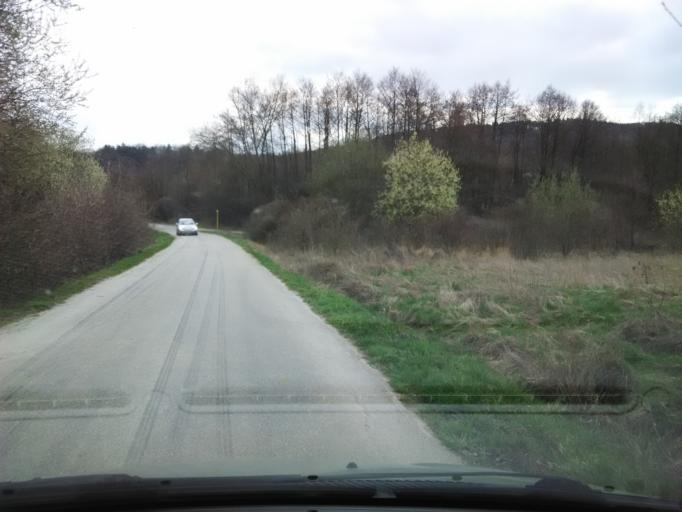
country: SK
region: Nitriansky
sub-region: Okres Nitra
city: Nitra
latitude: 48.3946
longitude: 18.2075
